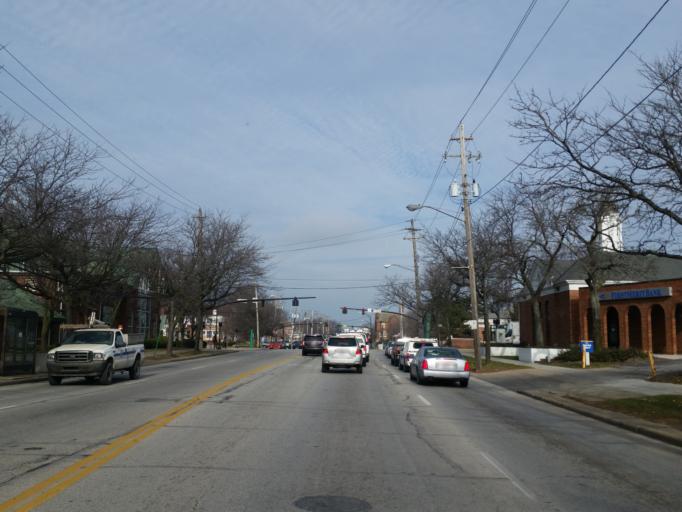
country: US
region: Ohio
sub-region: Cuyahoga County
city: Shaker Heights
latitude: 41.4636
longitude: -81.5649
